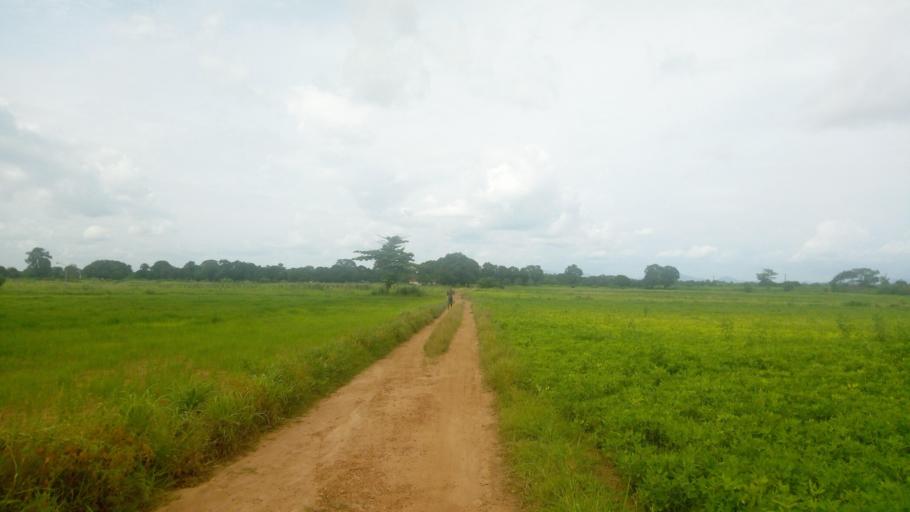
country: SL
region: Northern Province
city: Magburaka
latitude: 8.6744
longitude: -12.0157
